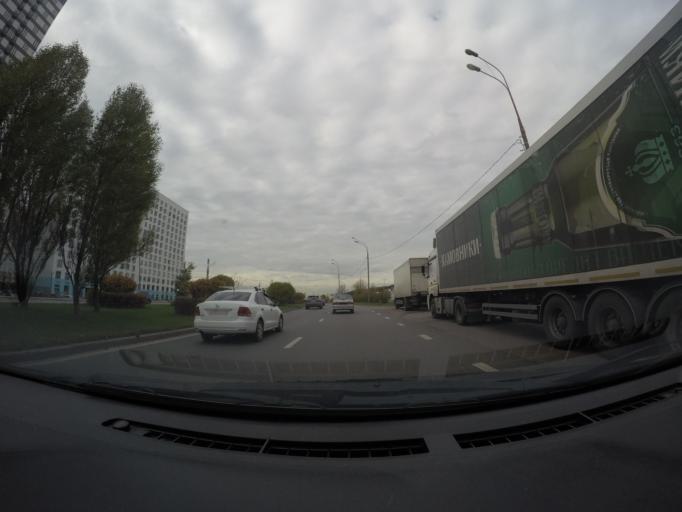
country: RU
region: Moskovskaya
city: Mytishchi
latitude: 55.9233
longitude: 37.7124
